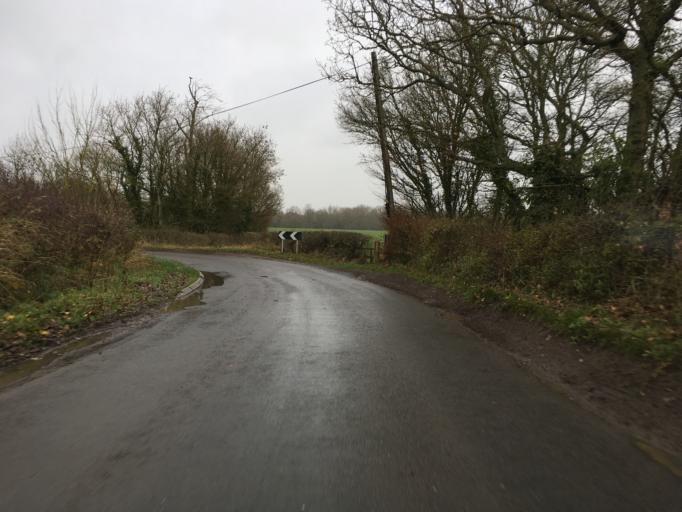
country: GB
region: England
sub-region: Wiltshire
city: Luckington
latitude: 51.5249
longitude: -2.2087
